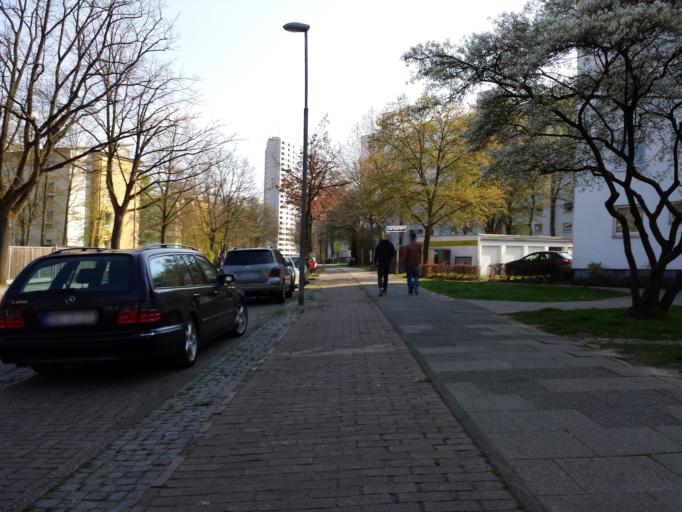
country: DE
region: Lower Saxony
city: Lilienthal
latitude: 53.0848
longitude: 8.8913
